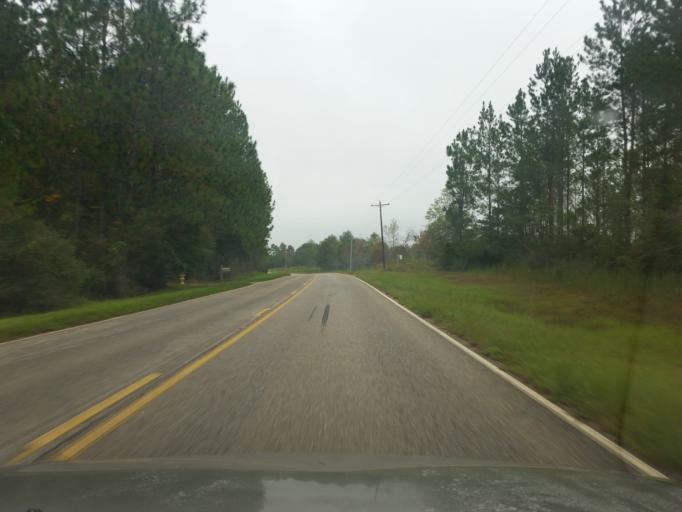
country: US
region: Florida
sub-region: Escambia County
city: Cantonment
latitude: 30.6523
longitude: -87.4502
